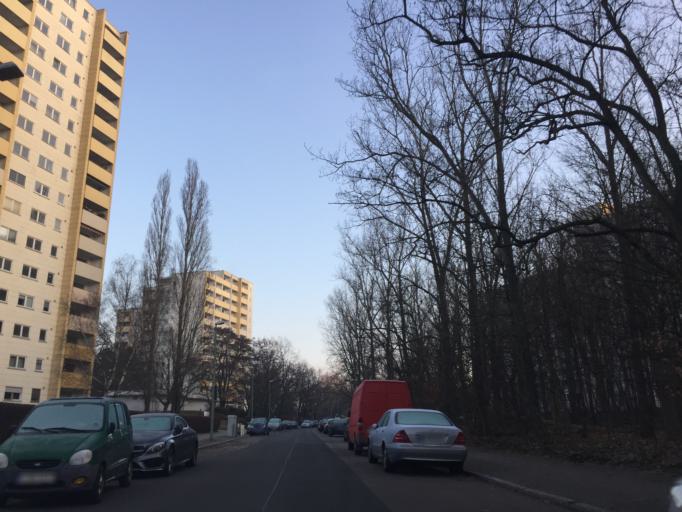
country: DE
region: Berlin
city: Haselhorst
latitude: 52.5097
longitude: 13.2194
